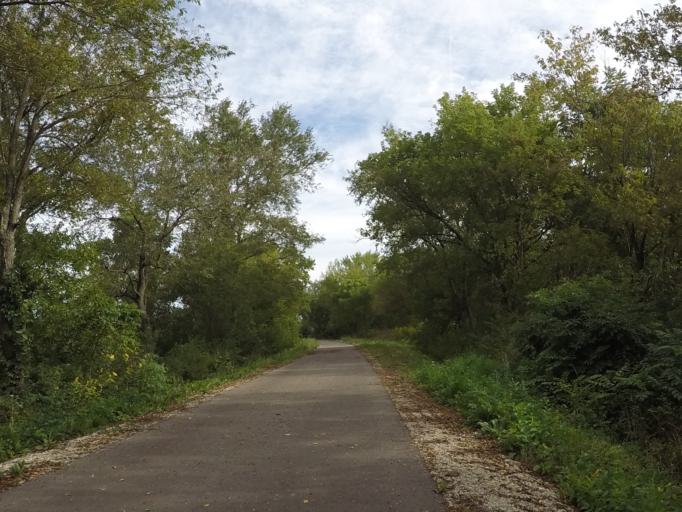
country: US
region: Wisconsin
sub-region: Sauk County
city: Prairie du Sac
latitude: 43.3449
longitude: -89.7412
